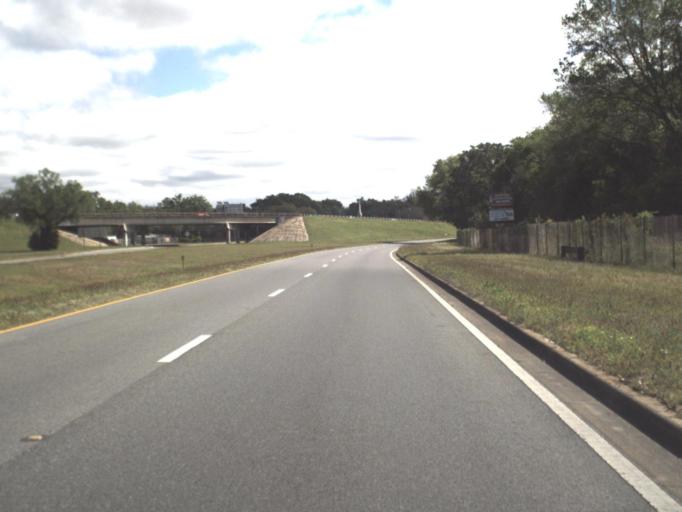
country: US
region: Florida
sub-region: Escambia County
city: West Pensacola
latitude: 30.4338
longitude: -87.2691
